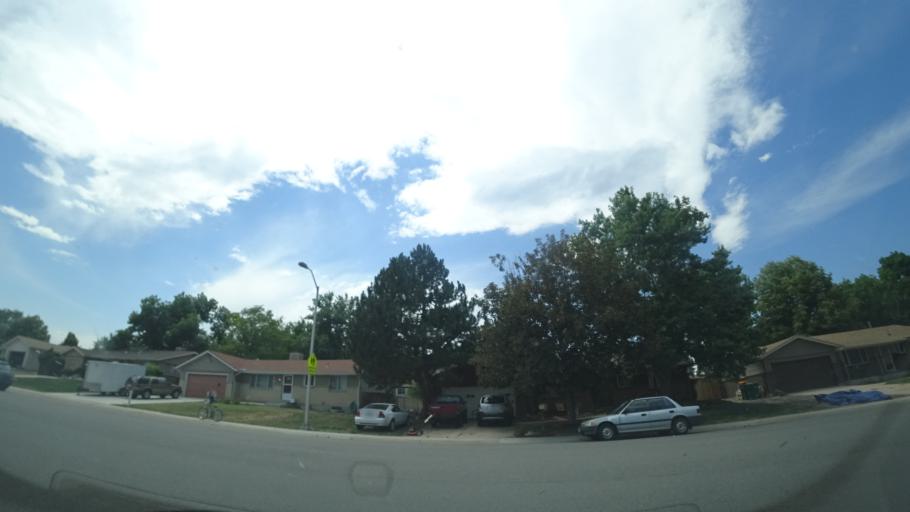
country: US
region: Colorado
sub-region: Jefferson County
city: Lakewood
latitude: 39.6940
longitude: -105.1045
